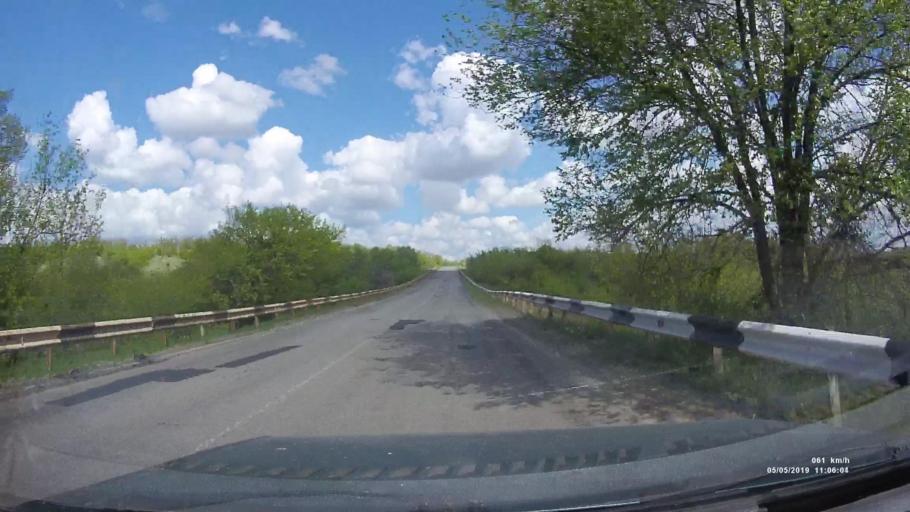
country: RU
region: Rostov
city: Ust'-Donetskiy
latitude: 47.7117
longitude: 40.9112
